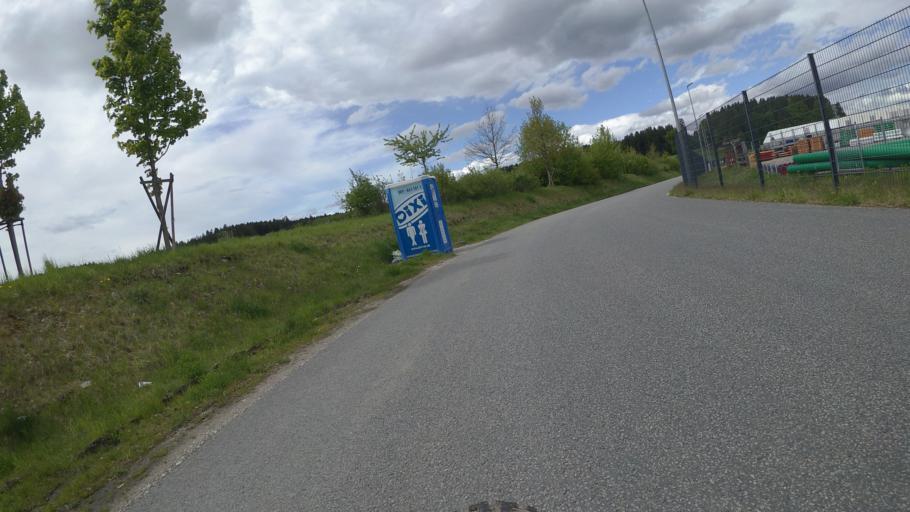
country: DE
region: Bavaria
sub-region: Upper Bavaria
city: Nussdorf
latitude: 47.8739
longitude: 12.5804
